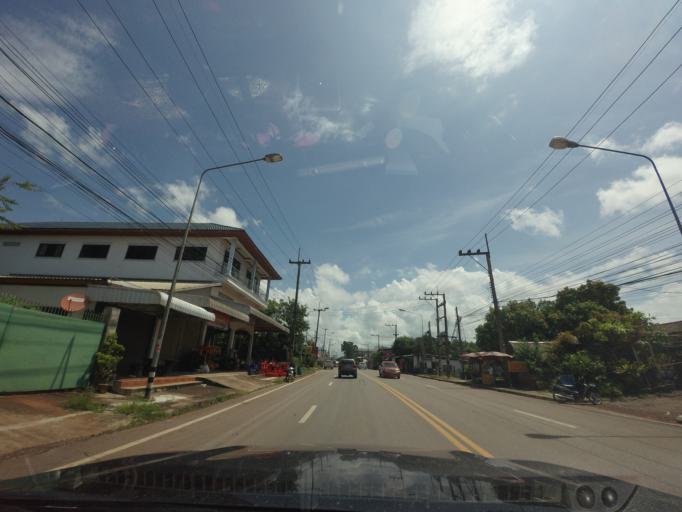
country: TH
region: Changwat Udon Thani
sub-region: Amphoe Ban Phue
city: Ban Phue
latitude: 17.6954
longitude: 102.4594
